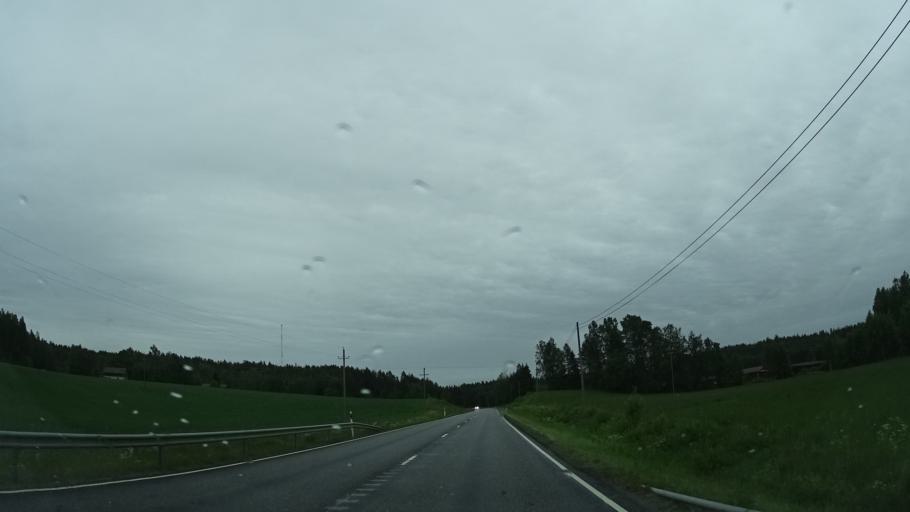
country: FI
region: Varsinais-Suomi
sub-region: Salo
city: Pernioe
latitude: 60.0888
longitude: 23.2279
